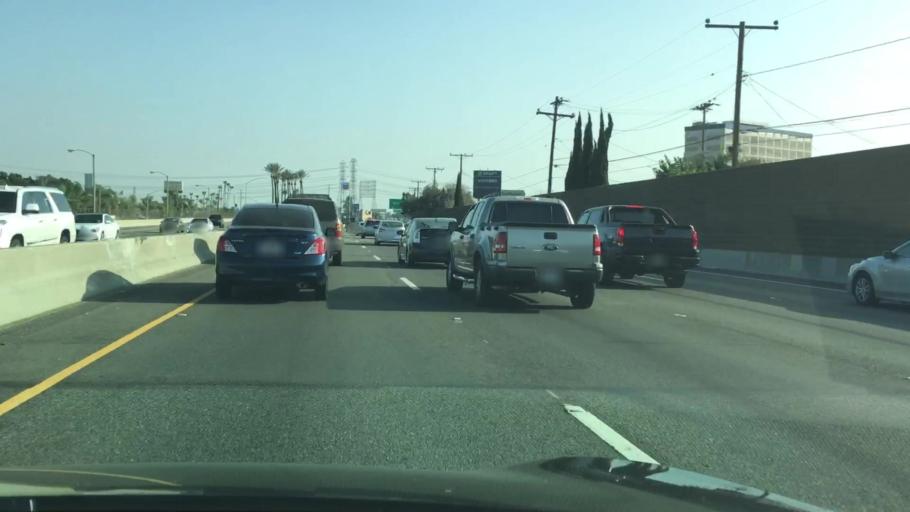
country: US
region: California
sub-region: Los Angeles County
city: Commerce
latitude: 34.0003
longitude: -118.1490
